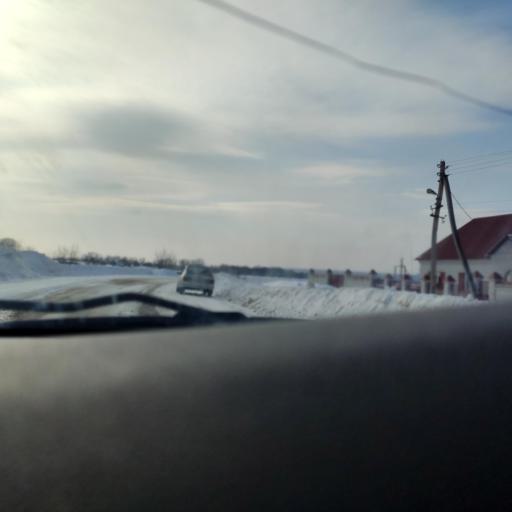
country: RU
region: Samara
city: Novokuybyshevsk
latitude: 53.2435
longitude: 49.9043
